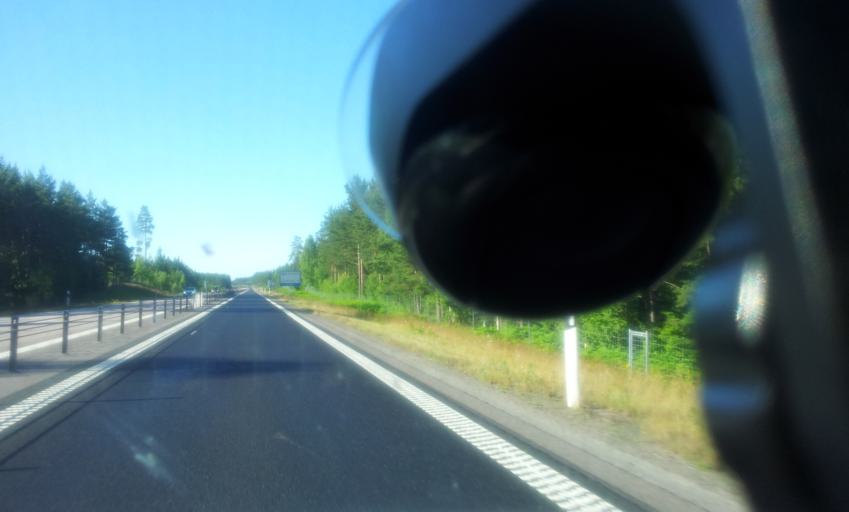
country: SE
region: Kalmar
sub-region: Torsas Kommun
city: Torsas
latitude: 56.4763
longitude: 16.0807
